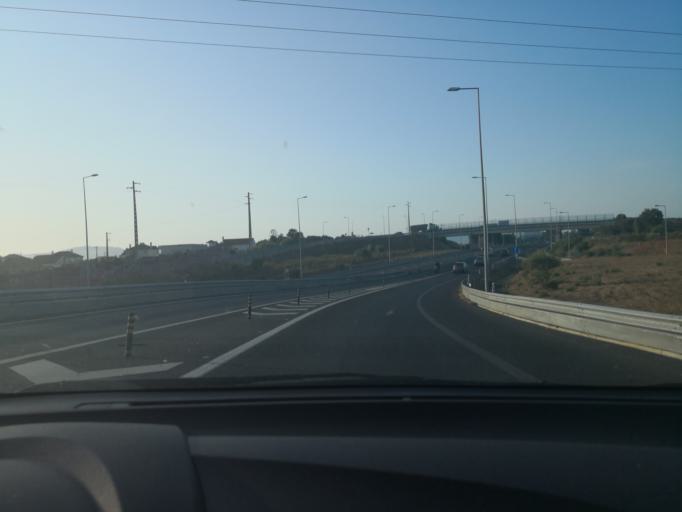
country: PT
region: Setubal
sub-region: Barreiro
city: Santo Antonio da Charneca
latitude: 38.5988
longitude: -9.0210
